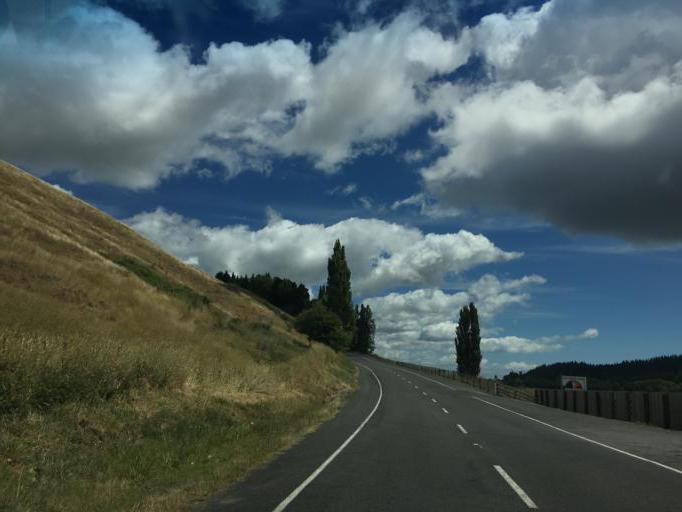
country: NZ
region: Hawke's Bay
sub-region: Hastings District
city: Hastings
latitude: -39.7044
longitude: 176.9314
